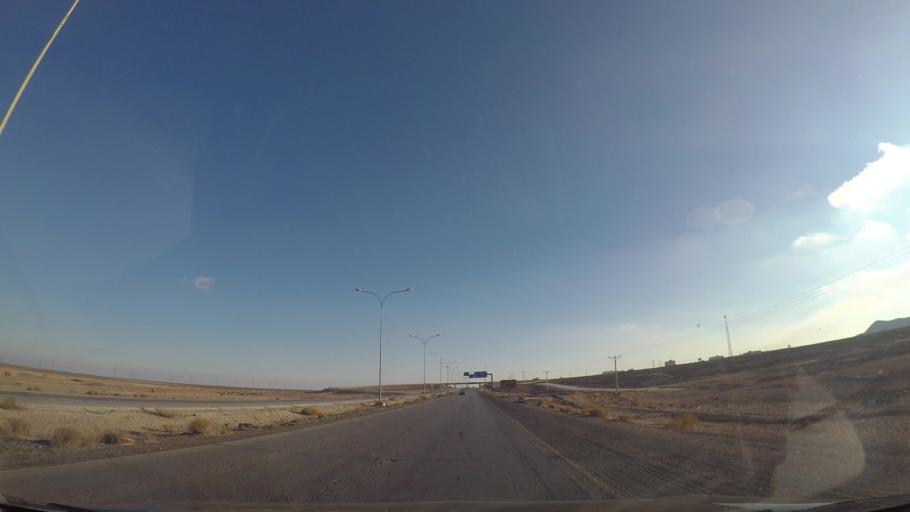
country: JO
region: Tafielah
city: Busayra
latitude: 30.5043
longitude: 35.7995
